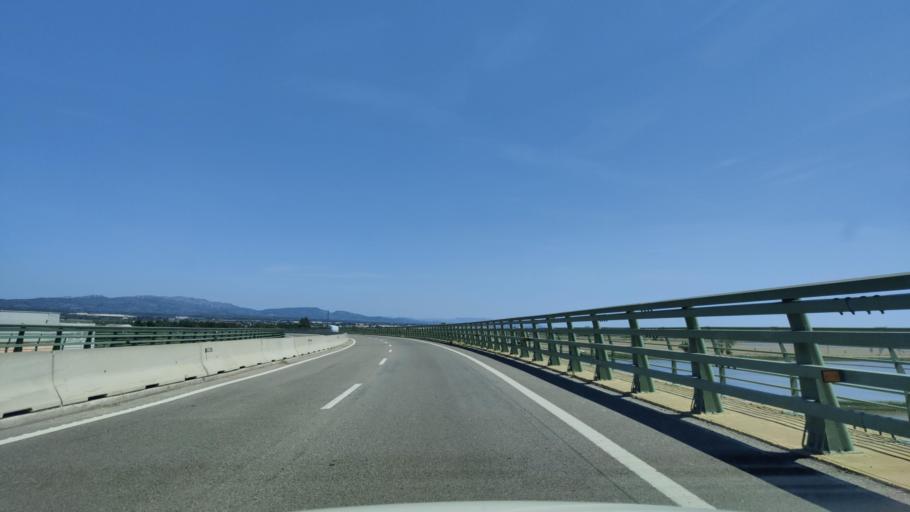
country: ES
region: Catalonia
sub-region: Provincia de Tarragona
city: Amposta
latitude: 40.7106
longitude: 0.5932
